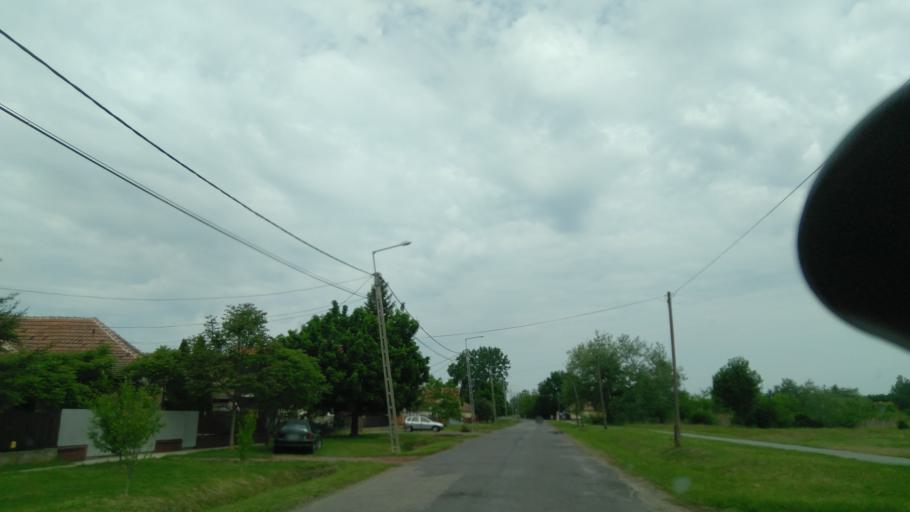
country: HU
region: Bekes
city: Szeghalom
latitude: 47.0313
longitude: 21.1664
